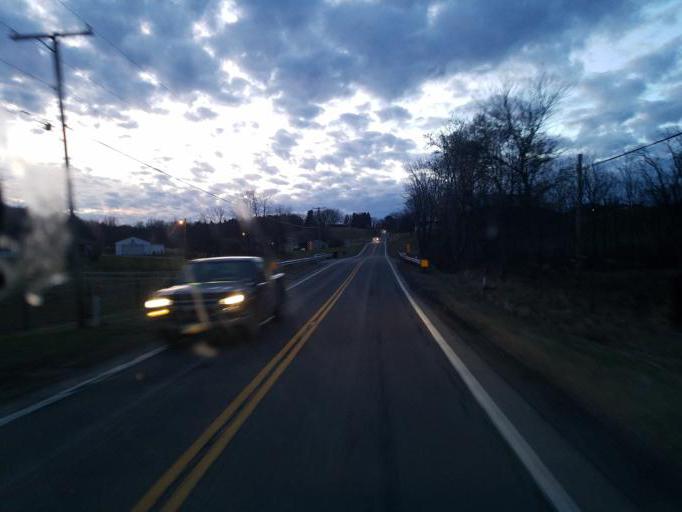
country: US
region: Ohio
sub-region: Knox County
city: Gambier
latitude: 40.2807
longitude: -82.3050
